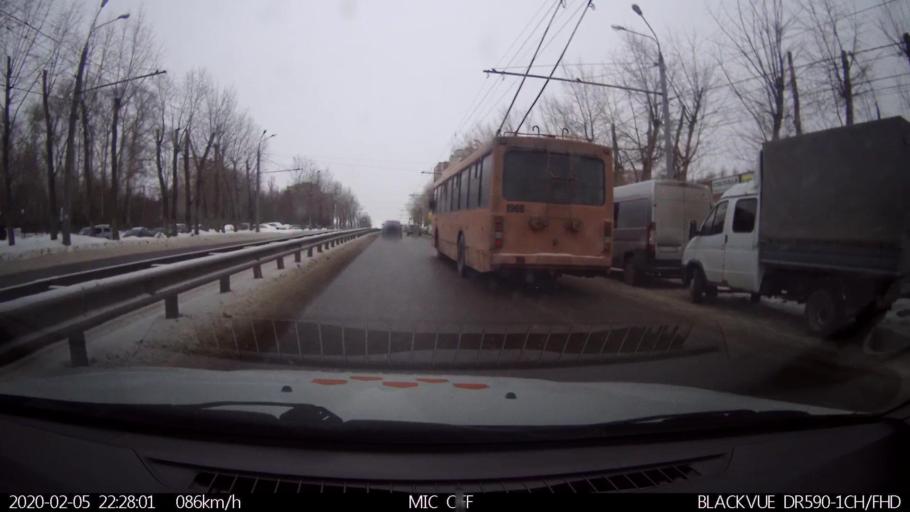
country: RU
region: Nizjnij Novgorod
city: Imeni Stepana Razina
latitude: 54.7604
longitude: 44.1251
